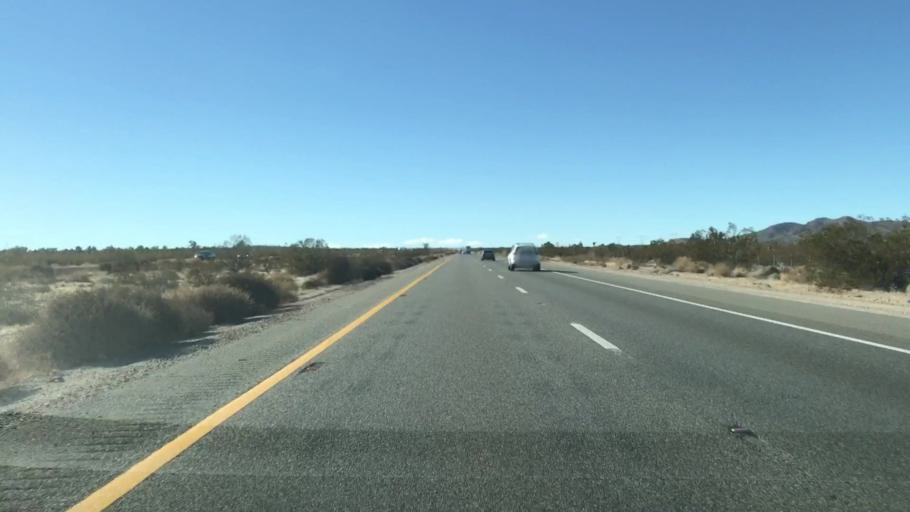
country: US
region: Nevada
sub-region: Clark County
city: Sandy Valley
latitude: 35.4150
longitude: -115.7569
